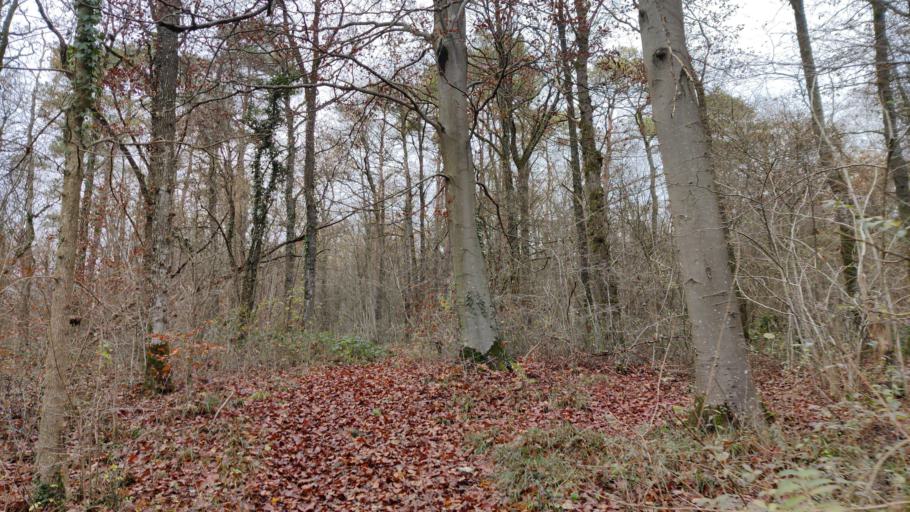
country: BE
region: Wallonia
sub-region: Province de Namur
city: Couvin
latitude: 50.0849
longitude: 4.6003
